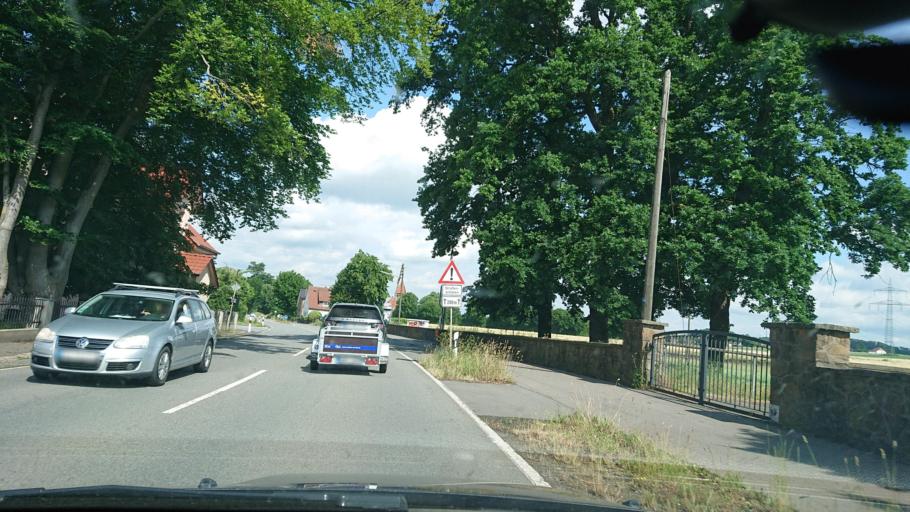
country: DE
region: North Rhine-Westphalia
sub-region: Regierungsbezirk Detmold
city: Hiddenhausen
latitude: 52.1598
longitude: 8.6398
